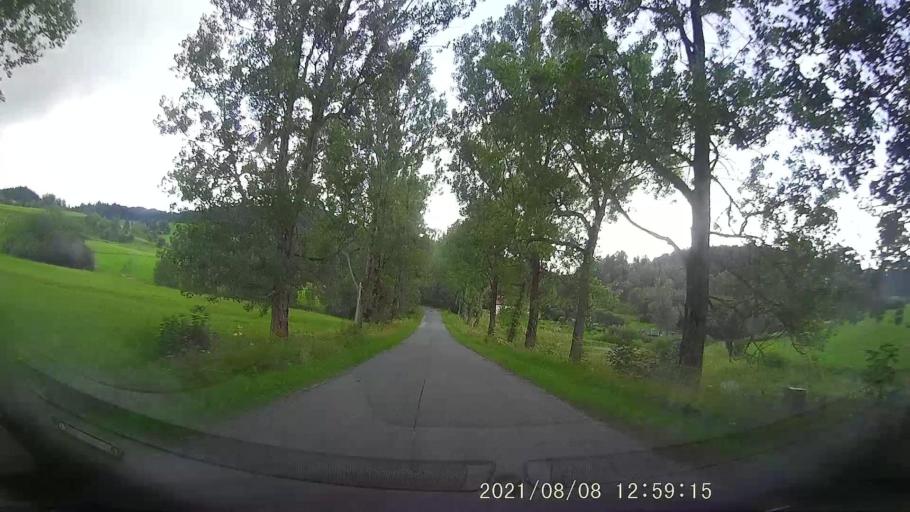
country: PL
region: Lower Silesian Voivodeship
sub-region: Powiat klodzki
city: Duszniki-Zdroj
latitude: 50.4096
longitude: 16.3516
